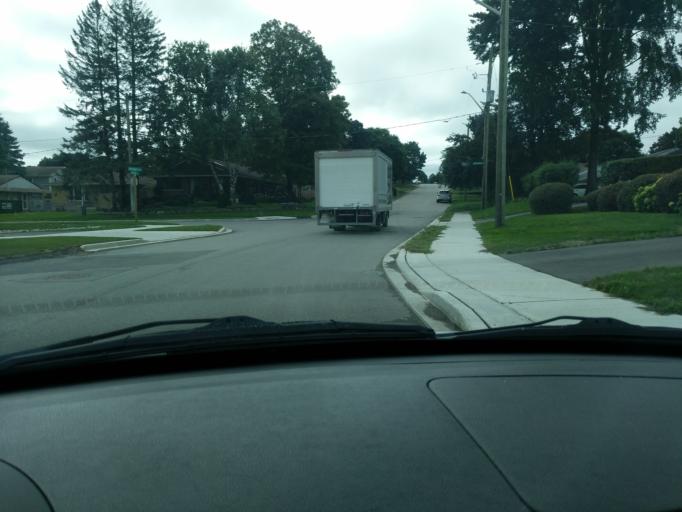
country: CA
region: Ontario
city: Cambridge
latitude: 43.4233
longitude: -80.3169
